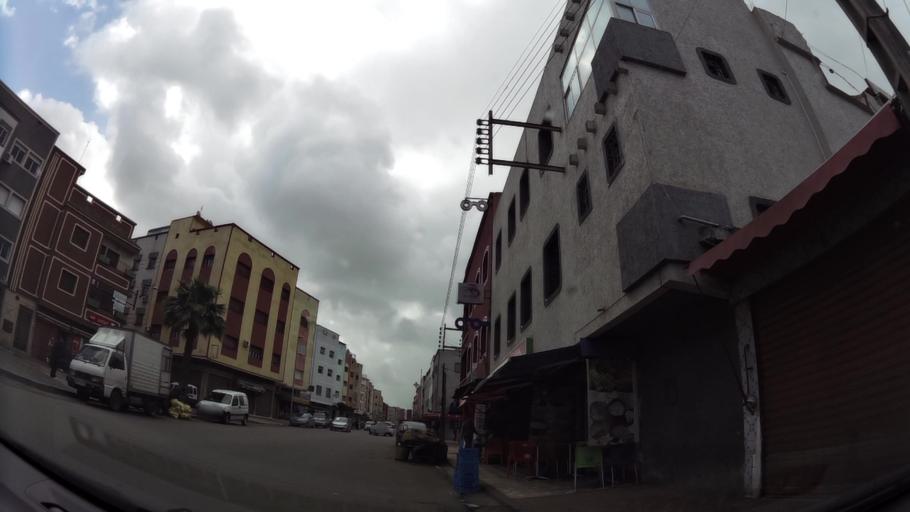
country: MA
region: Grand Casablanca
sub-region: Casablanca
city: Casablanca
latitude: 33.5382
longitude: -7.5984
